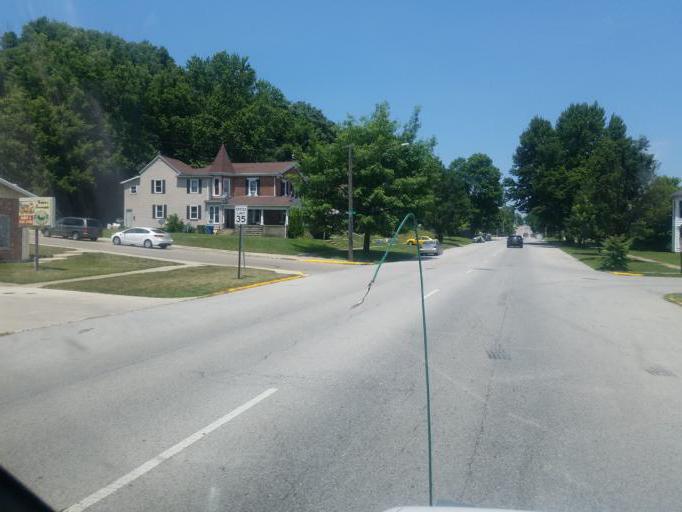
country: US
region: Ohio
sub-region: Shelby County
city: Sidney
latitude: 40.2901
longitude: -84.1551
